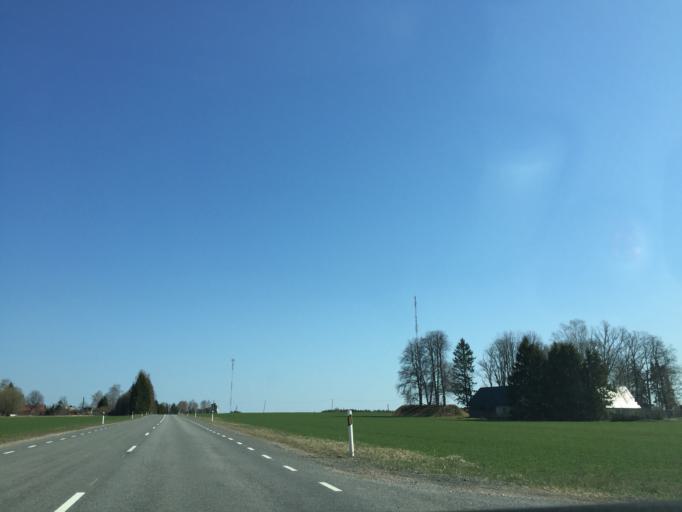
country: EE
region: Tartu
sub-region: Tartu linn
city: Tartu
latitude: 58.5065
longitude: 26.8841
